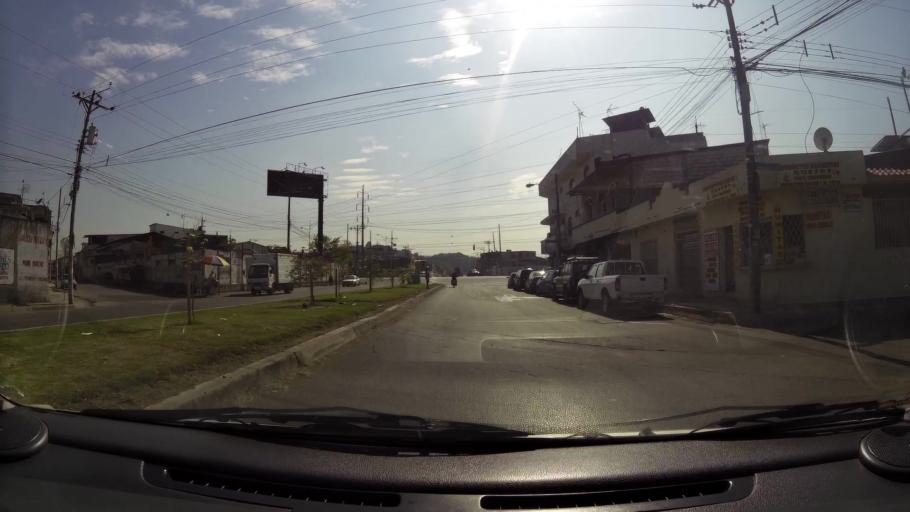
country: EC
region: Guayas
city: Eloy Alfaro
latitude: -2.0884
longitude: -79.9144
